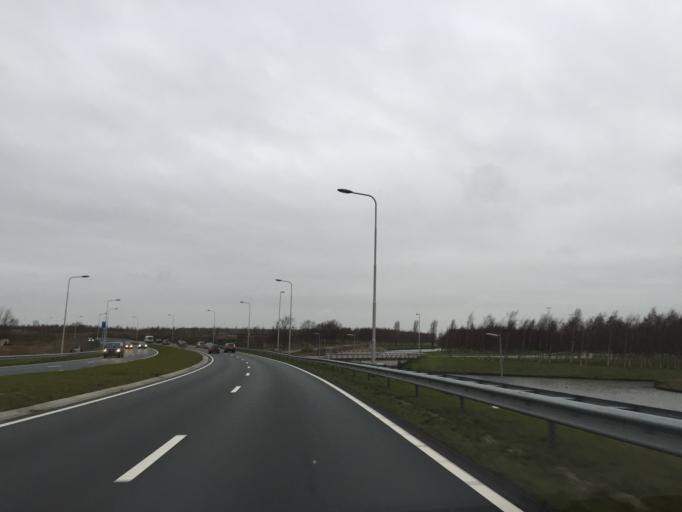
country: NL
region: North Holland
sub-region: Gemeente Aalsmeer
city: Aalsmeer
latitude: 52.2874
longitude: 4.7674
